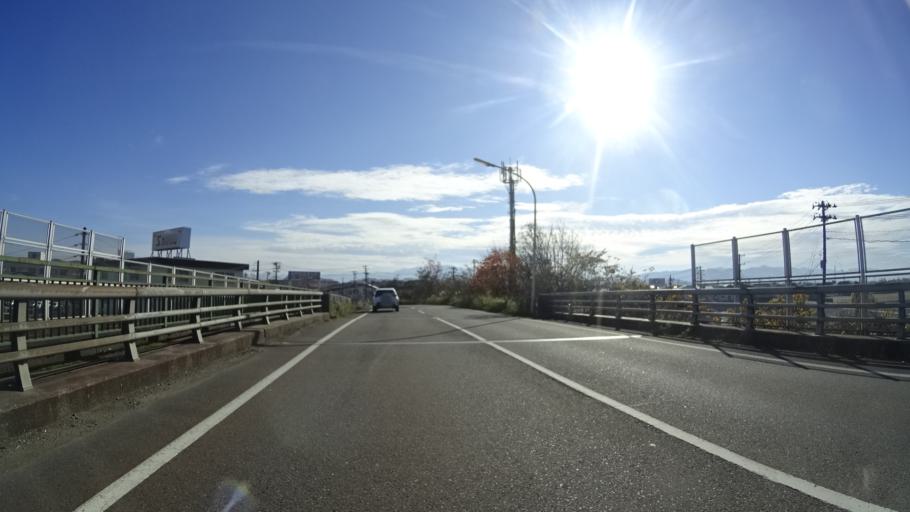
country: JP
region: Niigata
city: Mitsuke
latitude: 37.5377
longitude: 138.9029
